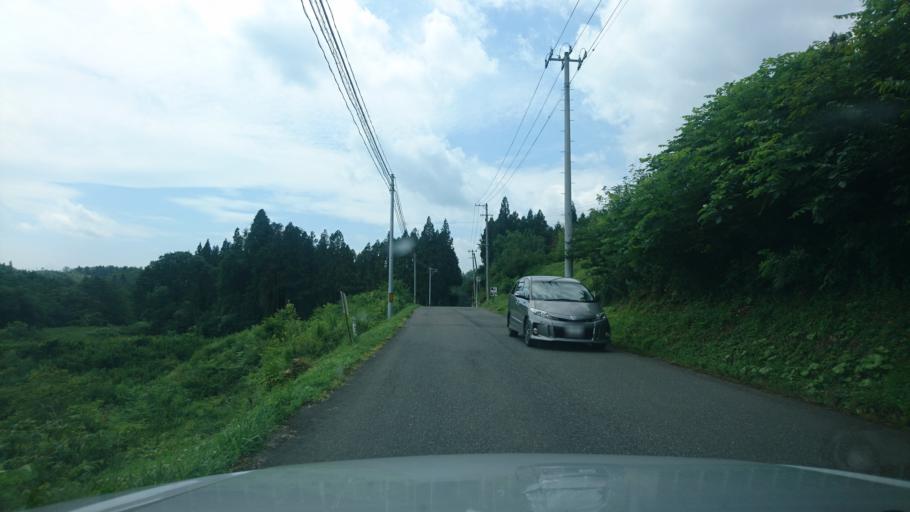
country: JP
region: Iwate
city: Ichinoseki
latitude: 38.8146
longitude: 140.9275
